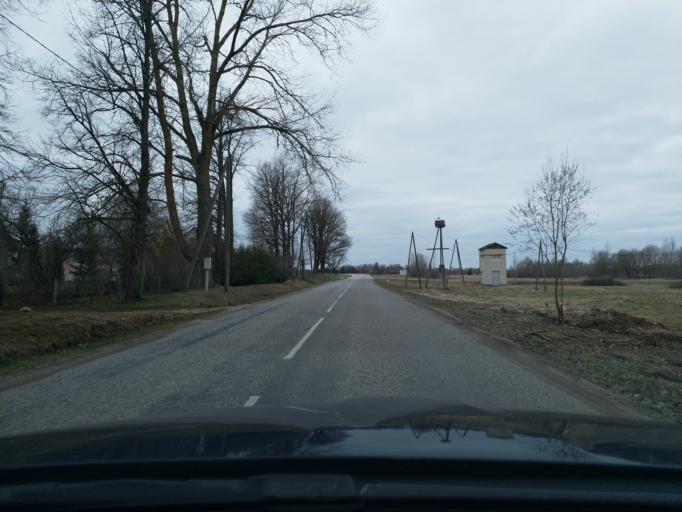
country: LV
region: Talsu Rajons
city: Sabile
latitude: 56.9239
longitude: 22.5588
